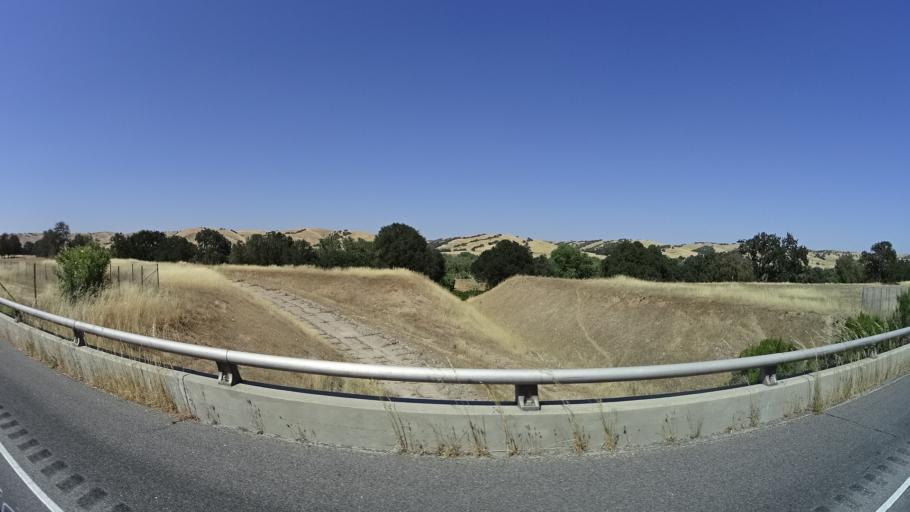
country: US
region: California
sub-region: San Luis Obispo County
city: San Miguel
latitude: 35.8452
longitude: -120.7613
